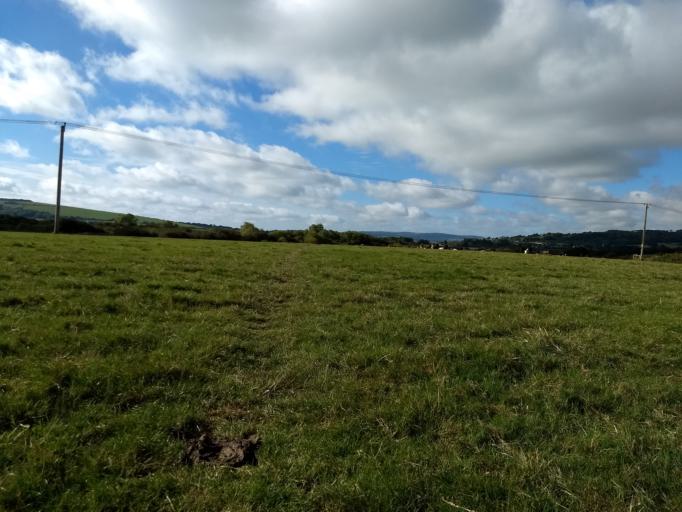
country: GB
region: England
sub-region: Isle of Wight
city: Brading
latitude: 50.6931
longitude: -1.1240
